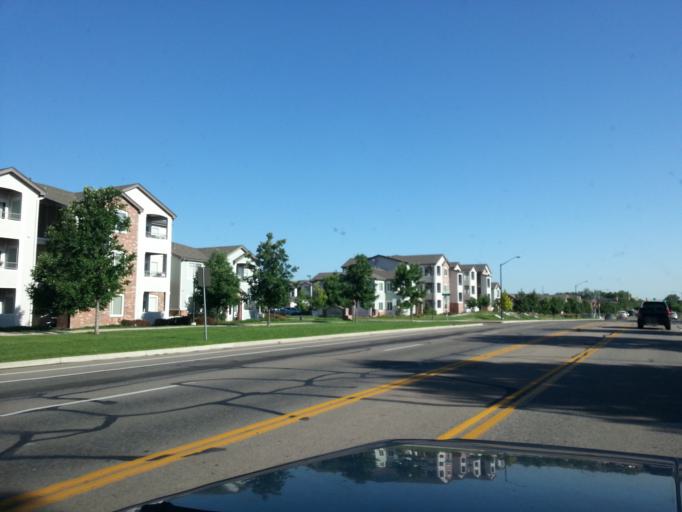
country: US
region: Colorado
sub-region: Larimer County
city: Fort Collins
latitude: 40.5287
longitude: -105.0393
